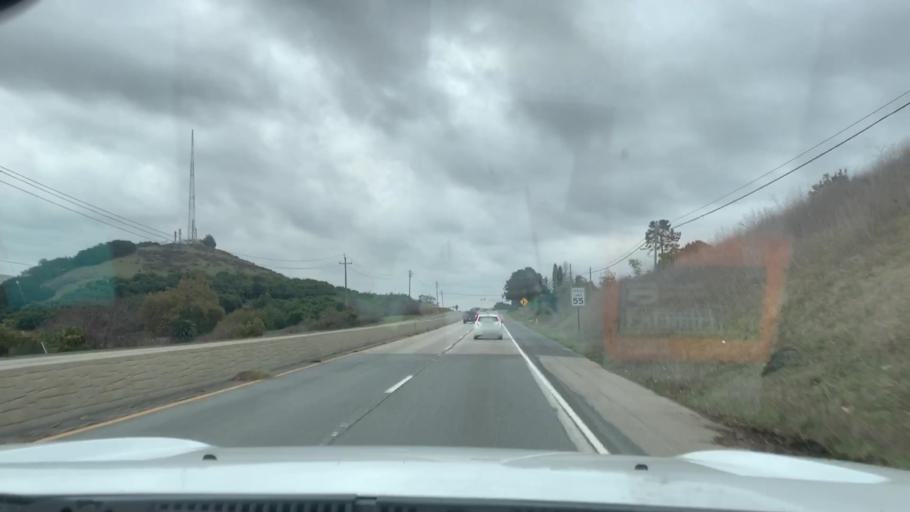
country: US
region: California
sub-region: San Luis Obispo County
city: San Luis Obispo
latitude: 35.3043
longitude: -120.6775
